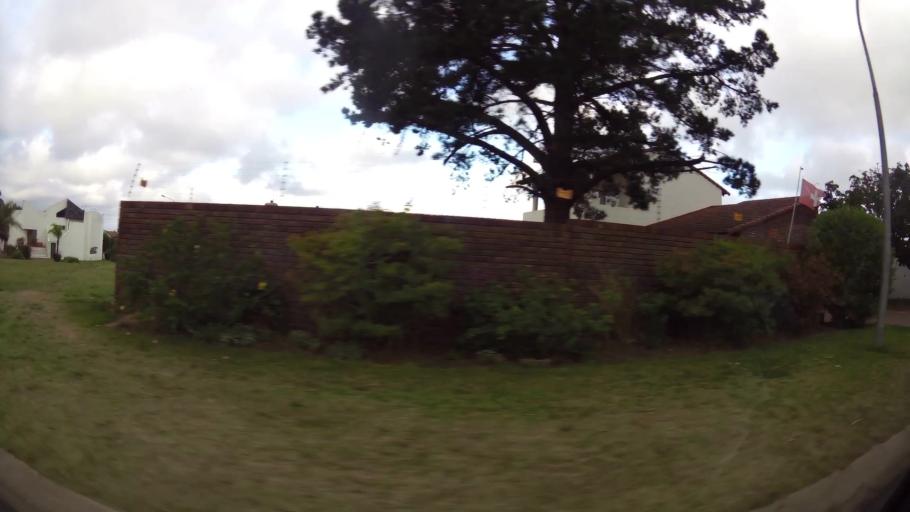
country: ZA
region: Western Cape
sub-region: Eden District Municipality
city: Plettenberg Bay
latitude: -34.0490
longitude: 23.3639
